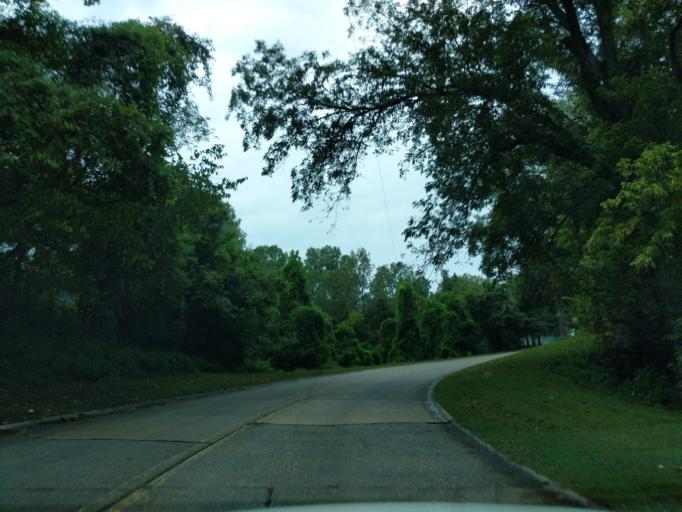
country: US
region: Mississippi
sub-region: Warren County
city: Vicksburg
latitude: 32.3173
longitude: -90.8944
